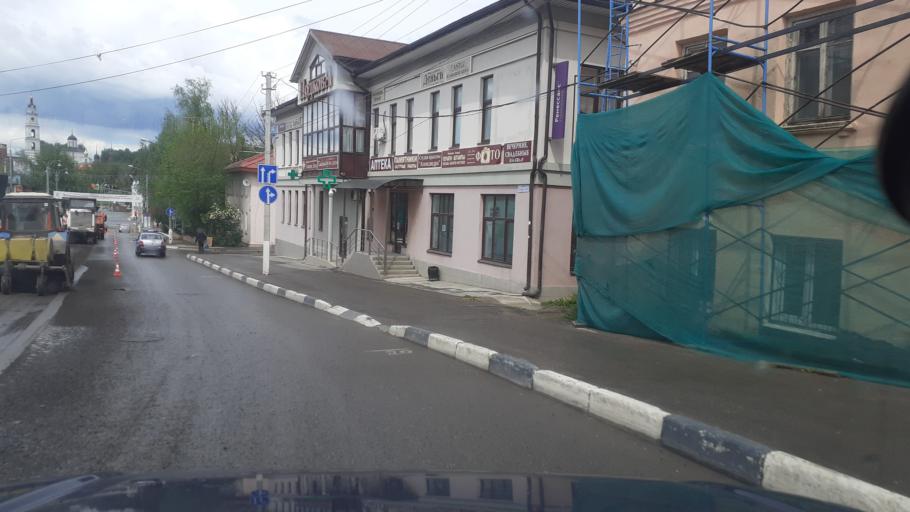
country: RU
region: Moskovskaya
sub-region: Volokolamskiy Rayon
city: Volokolamsk
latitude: 56.0331
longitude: 35.9593
